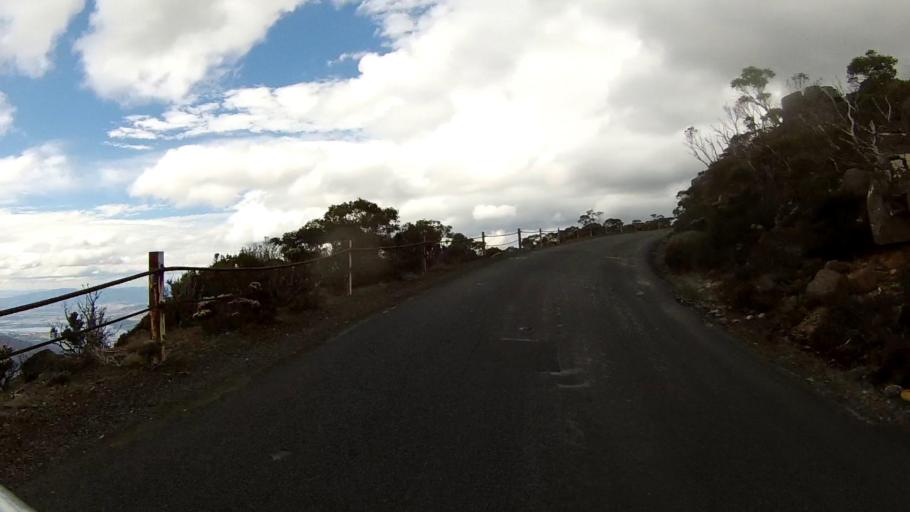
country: AU
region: Tasmania
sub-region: Glenorchy
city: West Moonah
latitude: -42.8916
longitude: 147.2269
